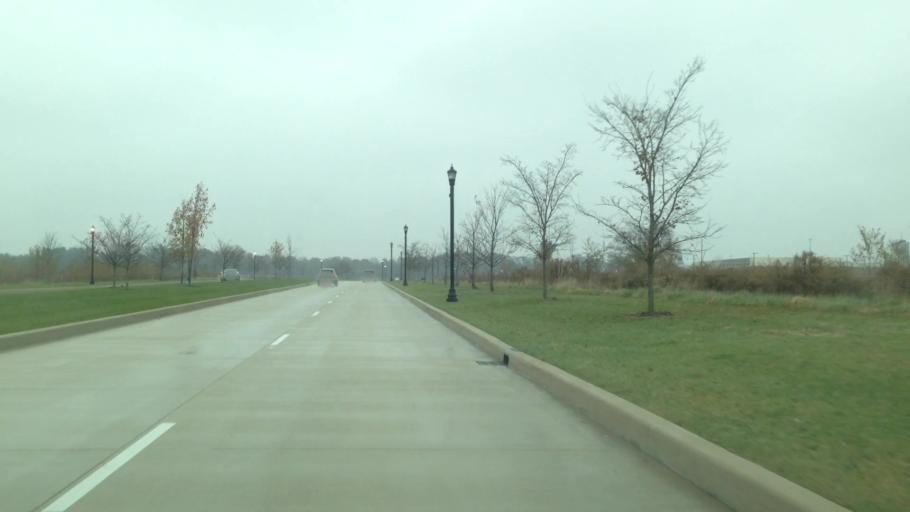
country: US
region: Indiana
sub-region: Saint Joseph County
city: Granger
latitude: 41.7299
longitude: -86.1511
